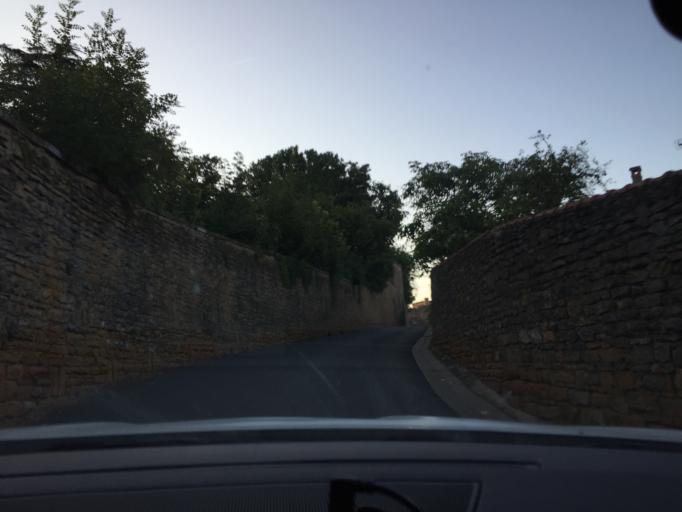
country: FR
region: Rhone-Alpes
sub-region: Departement du Rhone
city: Charnay
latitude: 45.8938
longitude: 4.6643
